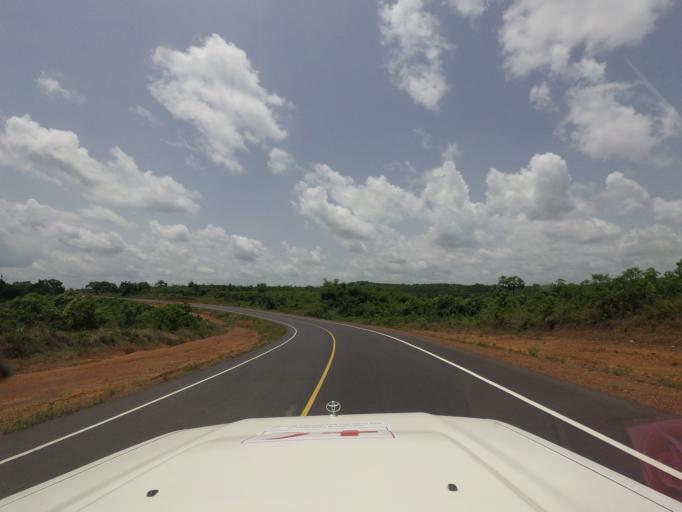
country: LR
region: Margibi
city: Kakata
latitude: 6.4770
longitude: -10.4024
